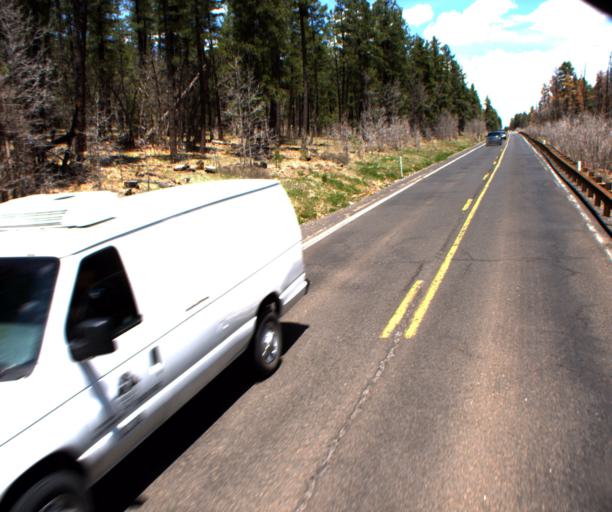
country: US
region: Arizona
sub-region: Coconino County
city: Kachina Village
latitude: 35.0508
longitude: -111.7329
